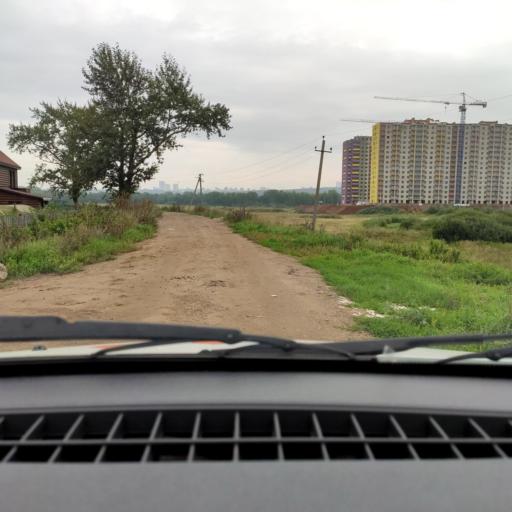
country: RU
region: Bashkortostan
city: Ufa
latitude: 54.7829
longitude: 55.9562
